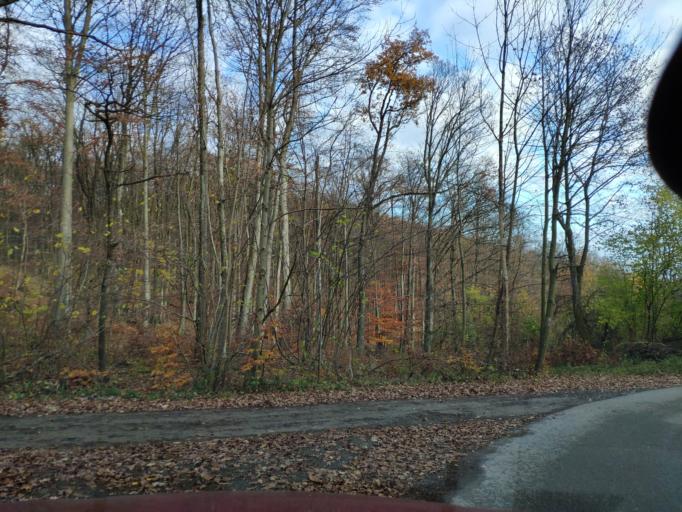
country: SK
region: Kosicky
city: Secovce
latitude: 48.5811
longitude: 21.4829
